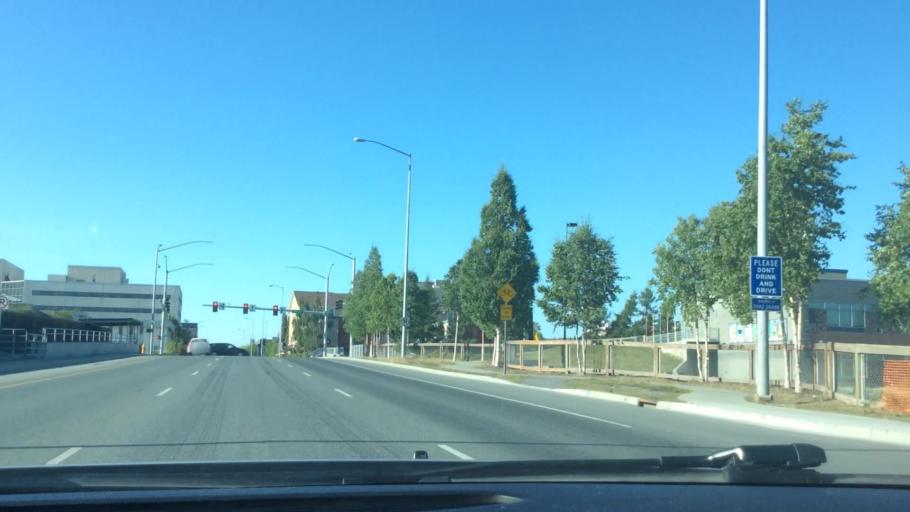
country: US
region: Alaska
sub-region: Anchorage Municipality
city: Anchorage
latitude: 61.2126
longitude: -149.8834
